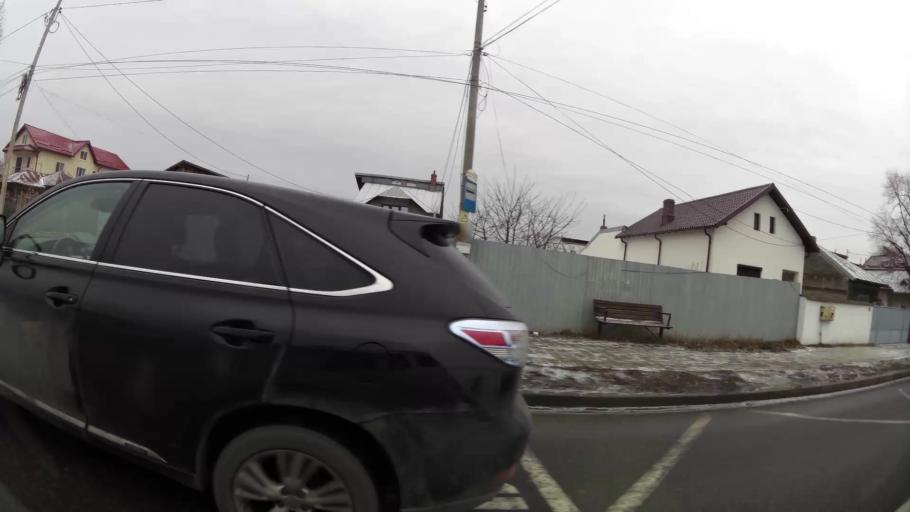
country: RO
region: Dambovita
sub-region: Comuna Ulmi
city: Ulmi
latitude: 44.9079
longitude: 25.4907
